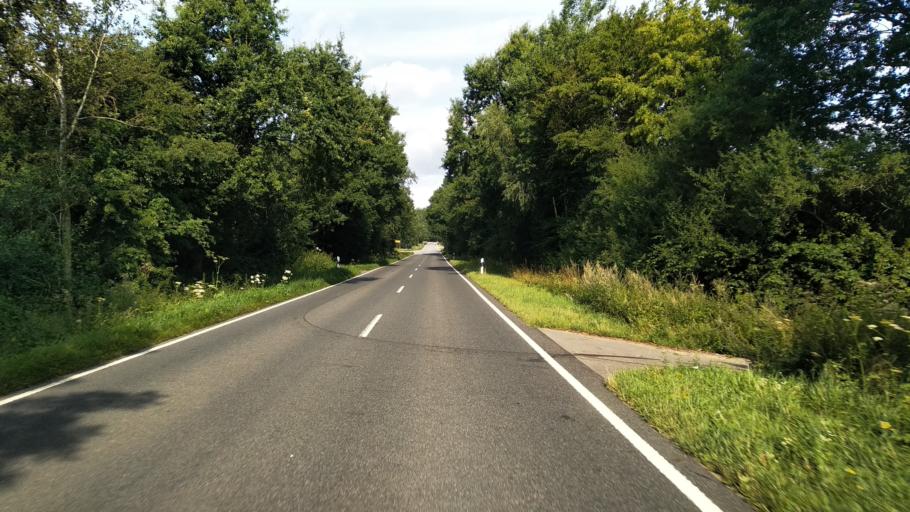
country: DE
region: Schleswig-Holstein
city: Selk
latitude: 54.4653
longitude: 9.5772
